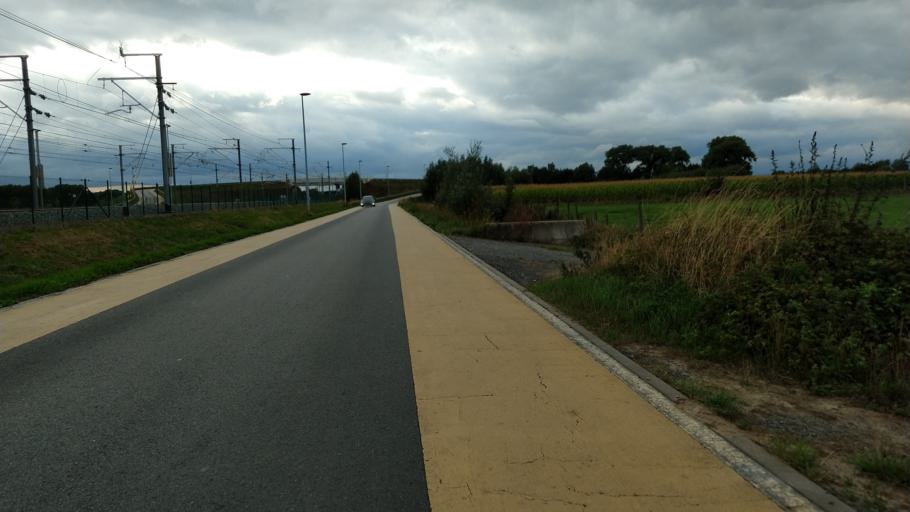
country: BE
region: Flanders
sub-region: Provincie Oost-Vlaanderen
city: Lovendegem
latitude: 51.0561
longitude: 3.6155
